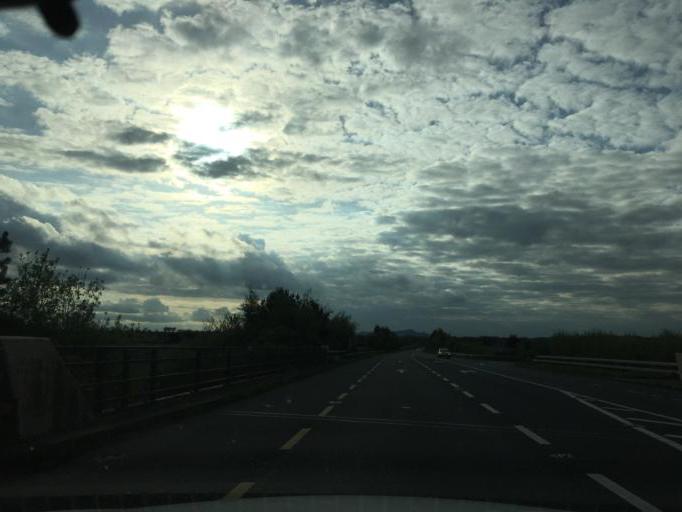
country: IE
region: Leinster
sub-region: Loch Garman
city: Enniscorthy
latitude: 52.3542
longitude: -6.6828
